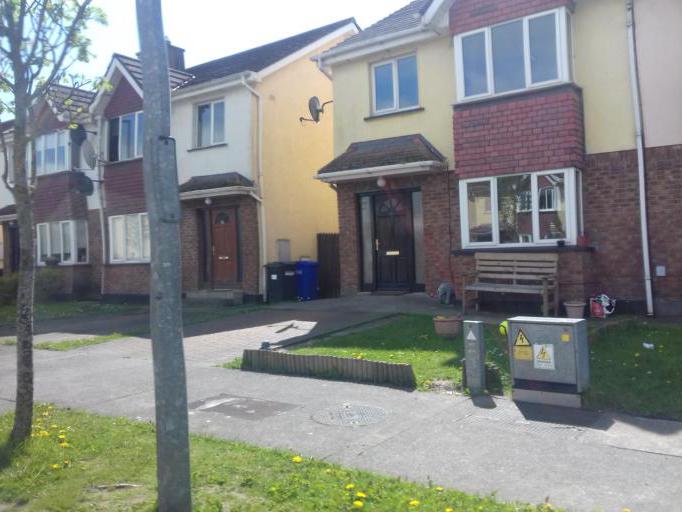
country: IE
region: Leinster
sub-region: Laois
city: Portlaoise
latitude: 53.0428
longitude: -7.3045
